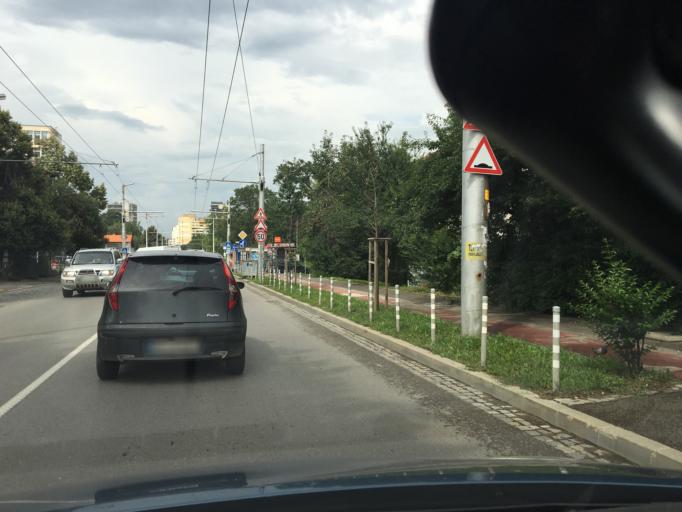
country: BG
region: Sofia-Capital
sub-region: Stolichna Obshtina
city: Sofia
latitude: 42.6644
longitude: 23.2749
